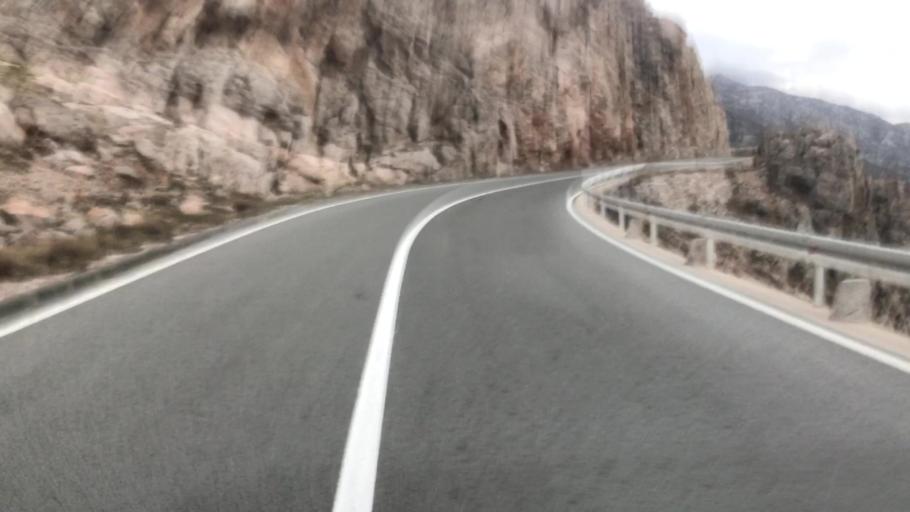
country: HR
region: Licko-Senjska
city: Karlobag
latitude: 44.5178
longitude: 15.0880
